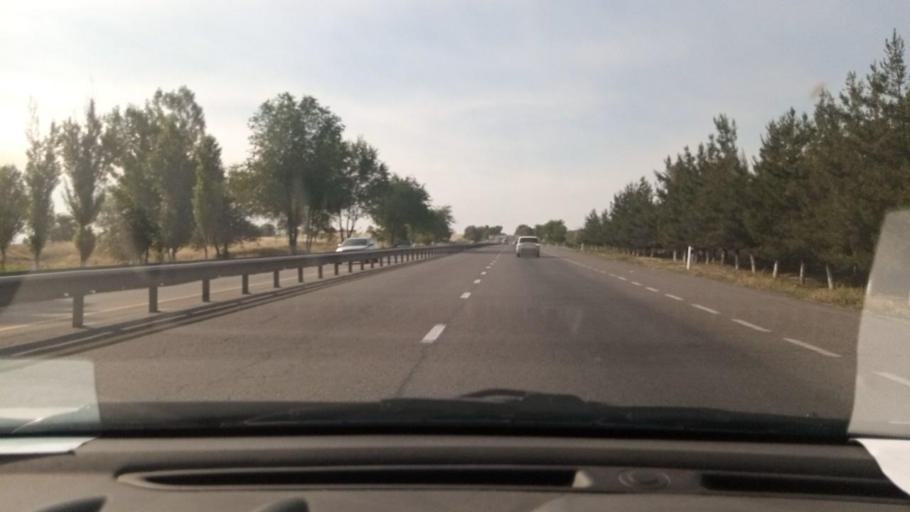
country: UZ
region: Toshkent
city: Tuytepa
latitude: 41.1165
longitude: 69.4446
